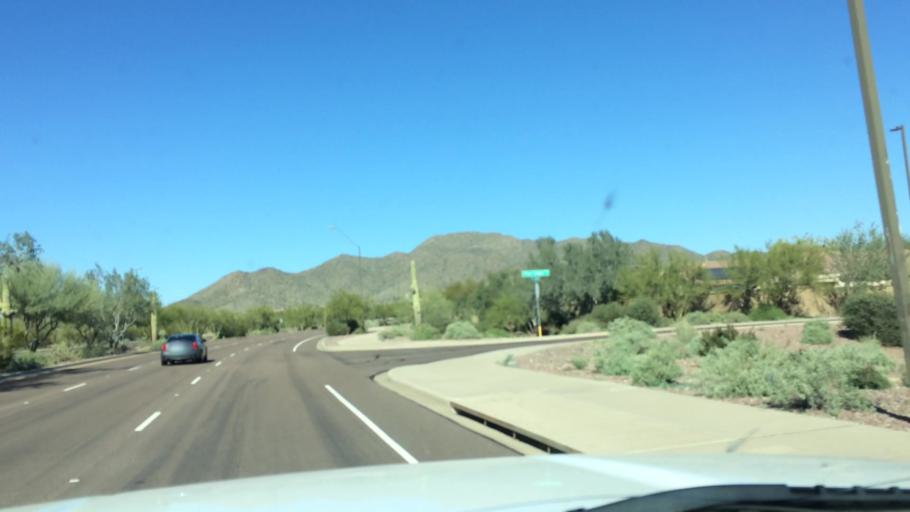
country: US
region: Arizona
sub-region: Maricopa County
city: Anthem
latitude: 33.8533
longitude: -112.1155
